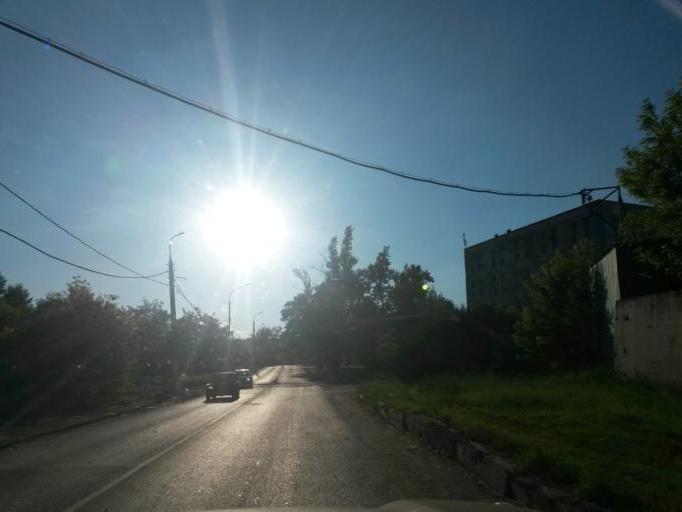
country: RU
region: Moscow
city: Annino
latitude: 55.5843
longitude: 37.6112
